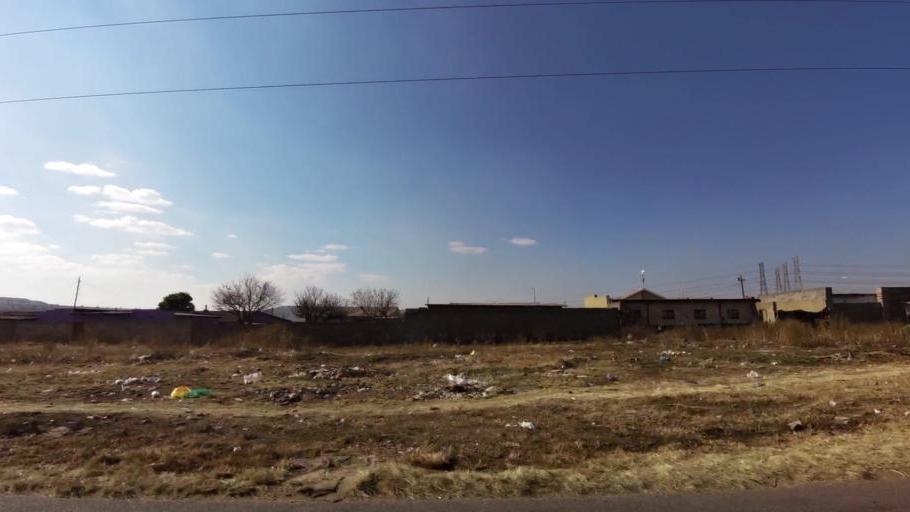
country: ZA
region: Gauteng
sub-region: City of Johannesburg Metropolitan Municipality
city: Soweto
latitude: -26.2368
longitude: 27.9374
